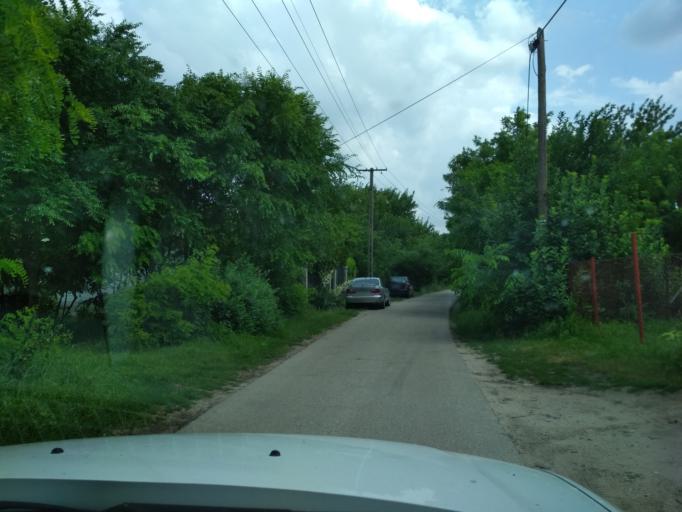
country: HU
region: Pest
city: Tapioszentmarton
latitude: 47.3707
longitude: 19.7593
